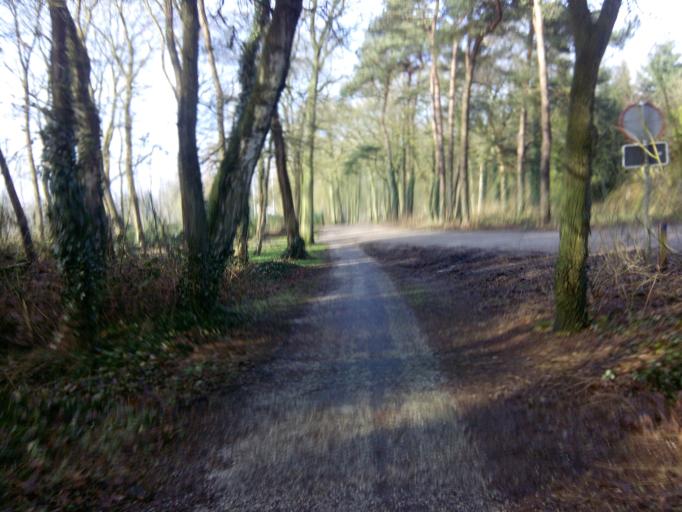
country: NL
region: Utrecht
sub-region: Gemeente Utrechtse Heuvelrug
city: Maarn
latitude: 52.0670
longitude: 5.3863
